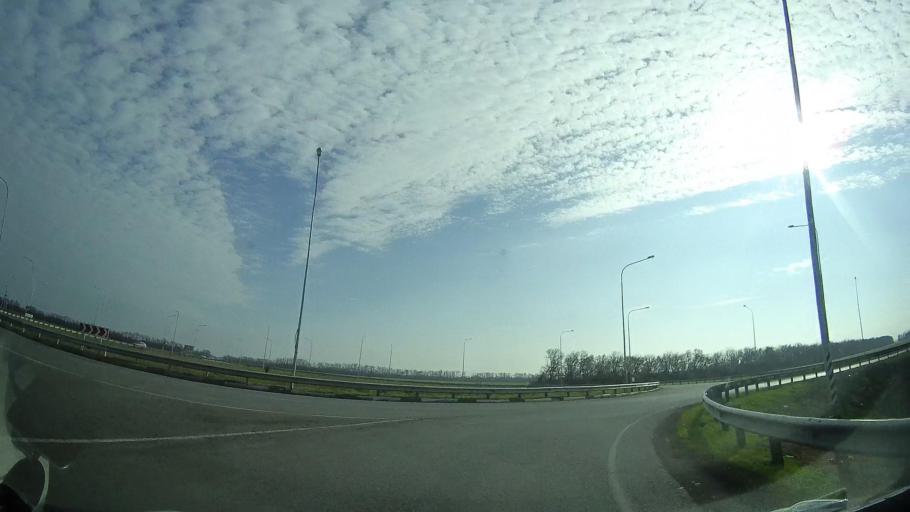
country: RU
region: Rostov
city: Tselina
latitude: 46.5264
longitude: 41.0792
